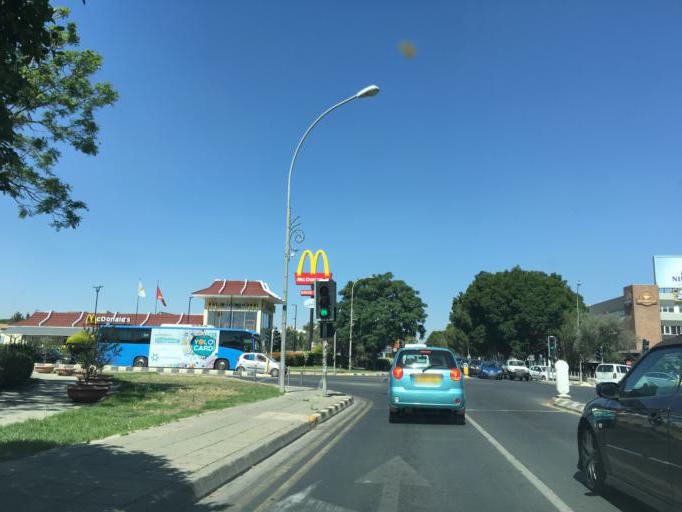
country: CY
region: Lefkosia
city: Nicosia
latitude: 35.1639
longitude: 33.3313
